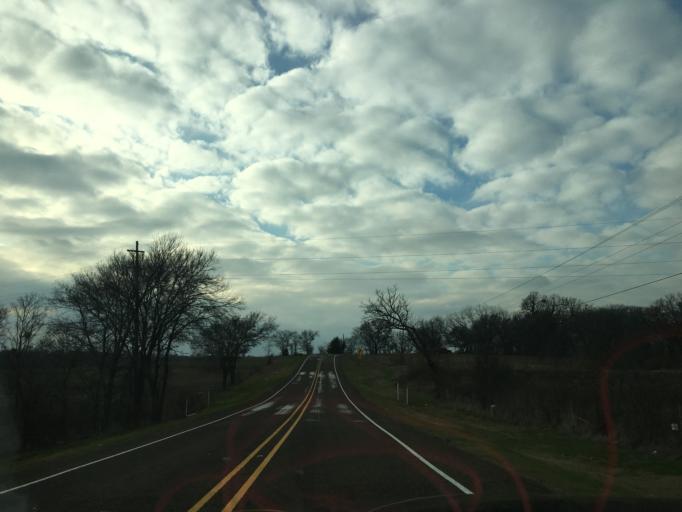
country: US
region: Texas
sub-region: Ellis County
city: Palmer
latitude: 32.4522
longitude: -96.7325
